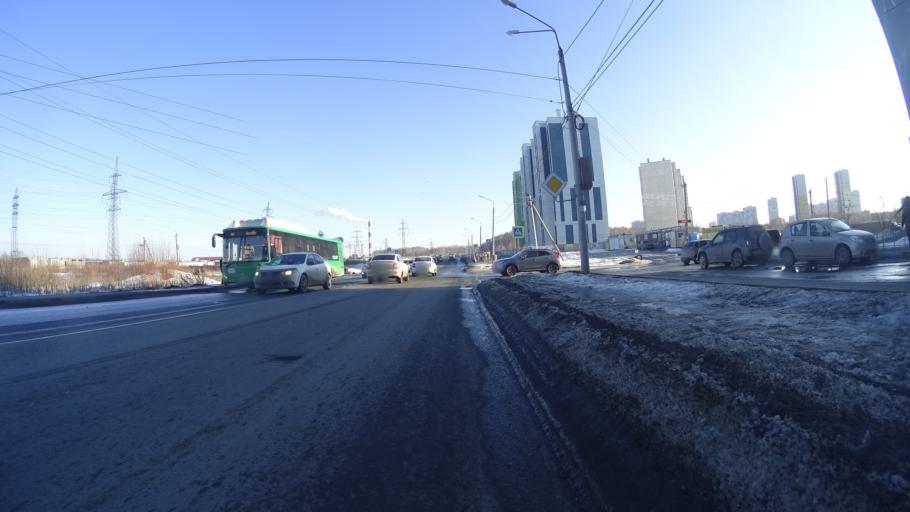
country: RU
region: Chelyabinsk
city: Roshchino
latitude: 55.2149
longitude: 61.3042
